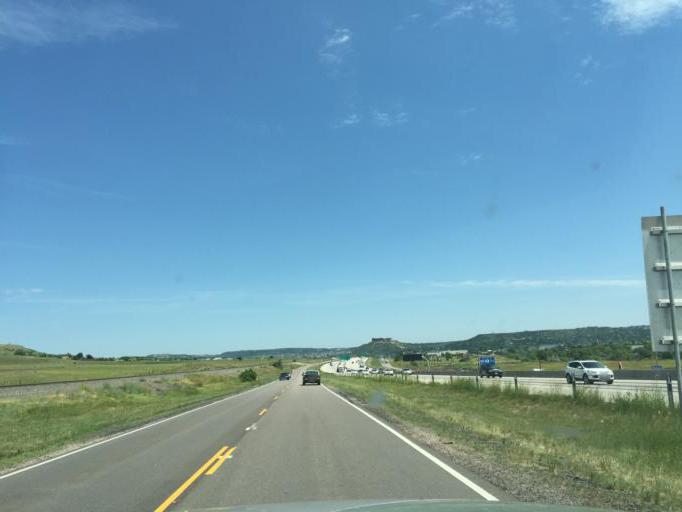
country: US
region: Colorado
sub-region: Douglas County
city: Castle Rock
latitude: 39.3477
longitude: -104.8732
